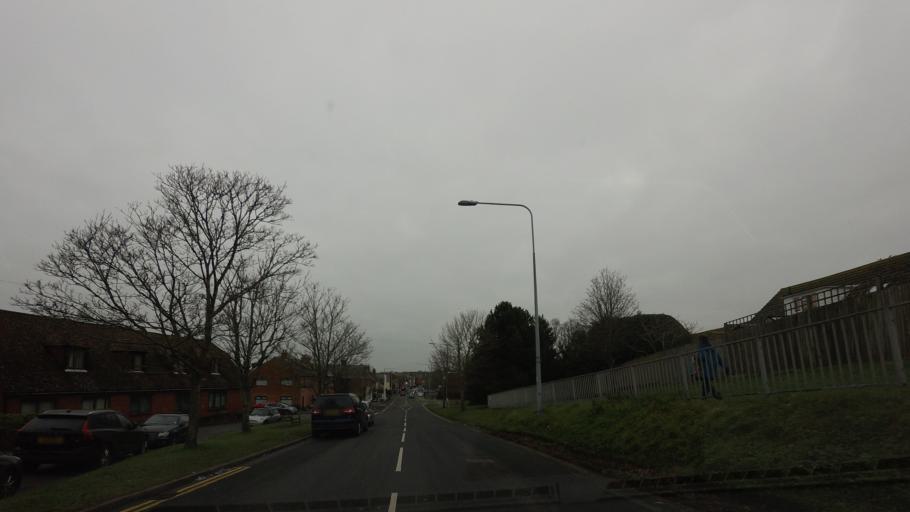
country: GB
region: England
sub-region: East Sussex
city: Bexhill-on-Sea
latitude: 50.8421
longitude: 0.4340
